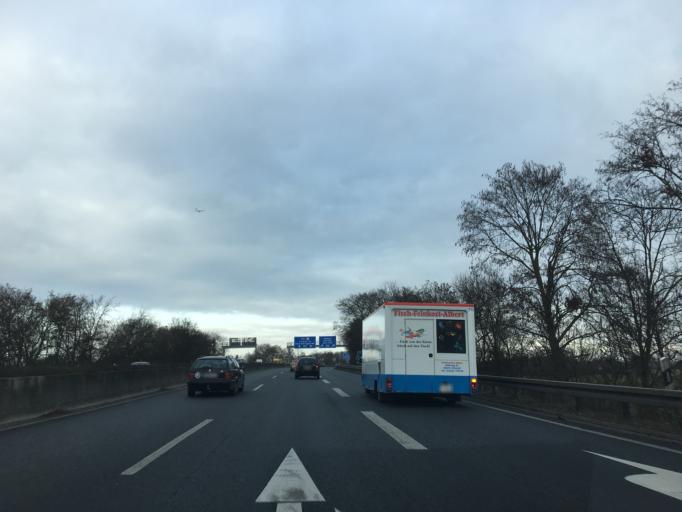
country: DE
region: North Rhine-Westphalia
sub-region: Regierungsbezirk Koln
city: Bonn
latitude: 50.7584
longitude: 7.1391
